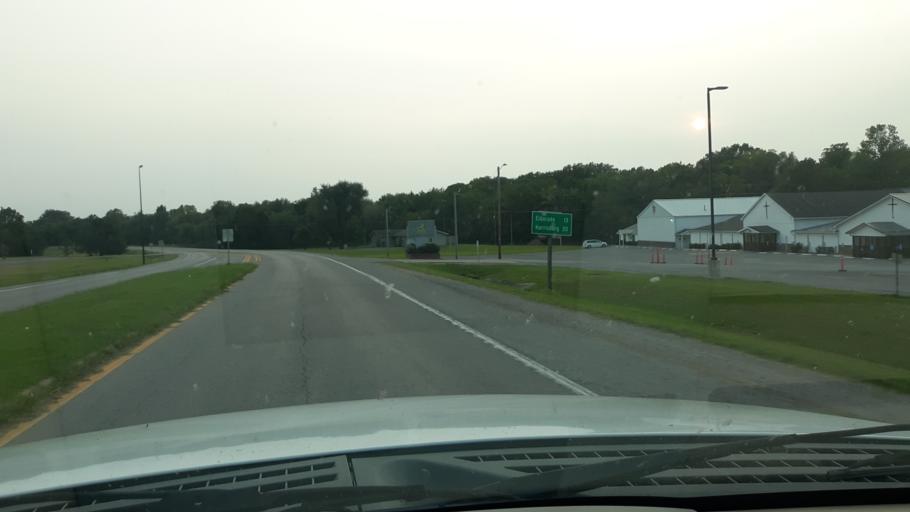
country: US
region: Illinois
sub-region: White County
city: Norris City
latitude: 37.9653
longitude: -88.3299
